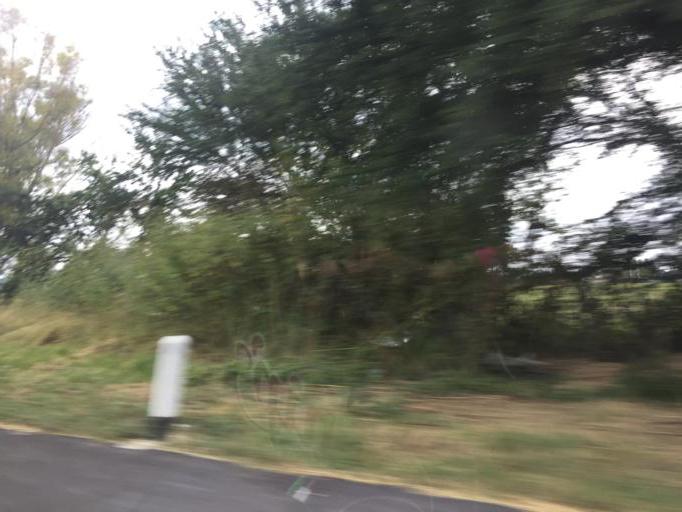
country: MX
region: Jalisco
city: Ocotlan
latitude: 20.3964
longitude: -102.7272
